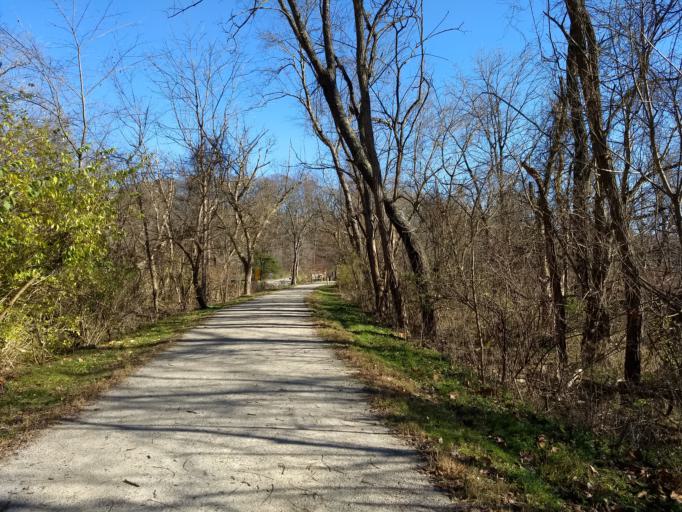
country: US
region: Pennsylvania
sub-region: Allegheny County
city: South Park Township
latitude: 40.2874
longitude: -79.9920
